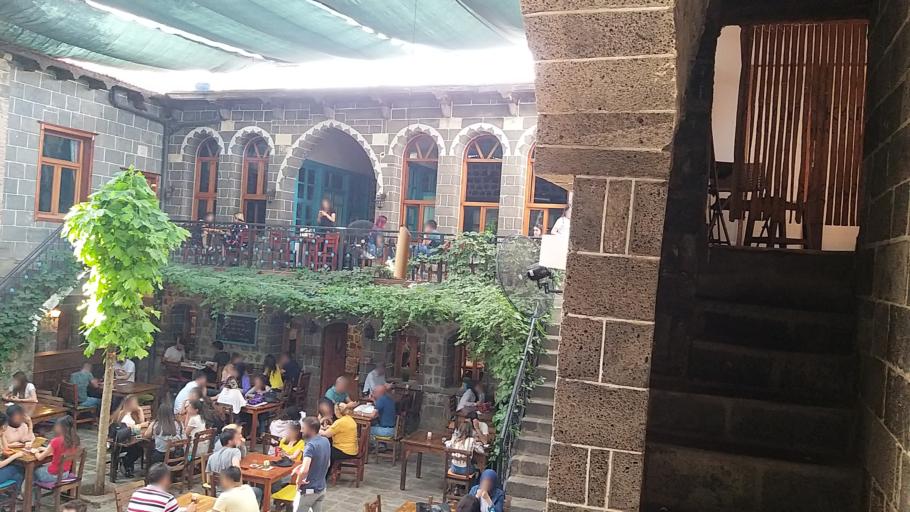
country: TR
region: Diyarbakir
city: Sur
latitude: 37.9154
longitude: 40.2390
